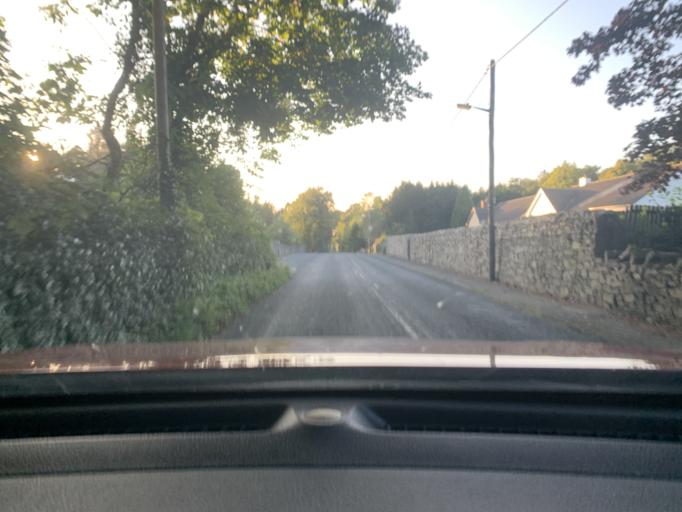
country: IE
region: Connaught
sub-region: Sligo
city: Sligo
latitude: 54.2727
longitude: -8.4307
